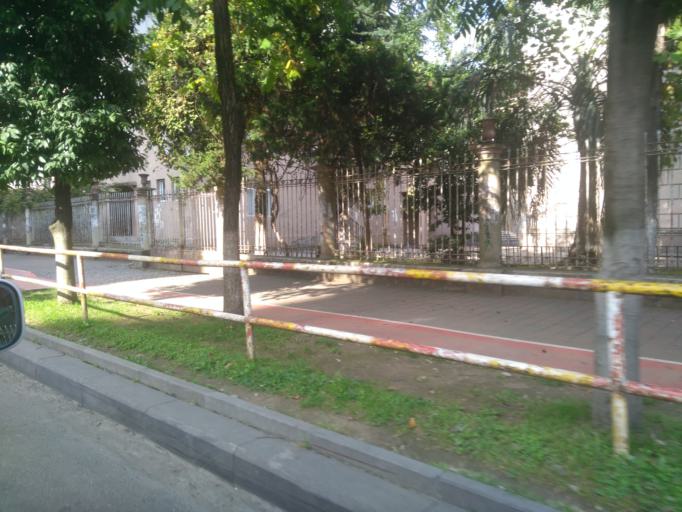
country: GE
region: Ajaria
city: Batumi
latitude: 41.6419
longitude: 41.6241
